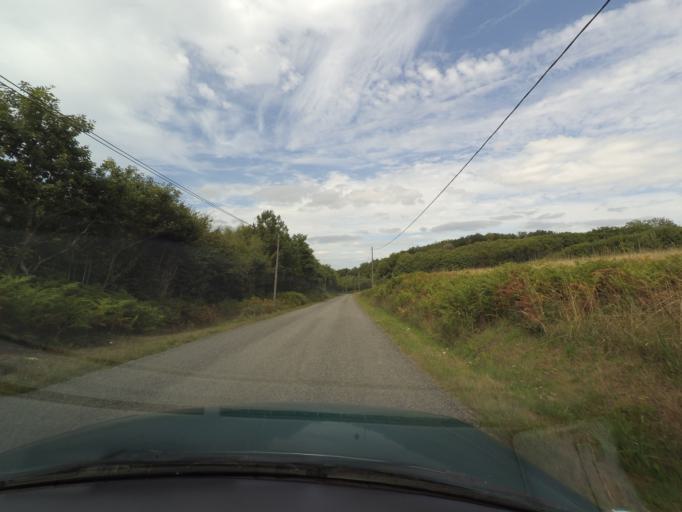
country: FR
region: Limousin
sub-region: Departement de la Haute-Vienne
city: Bussiere-Galant
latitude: 45.6566
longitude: 1.0772
